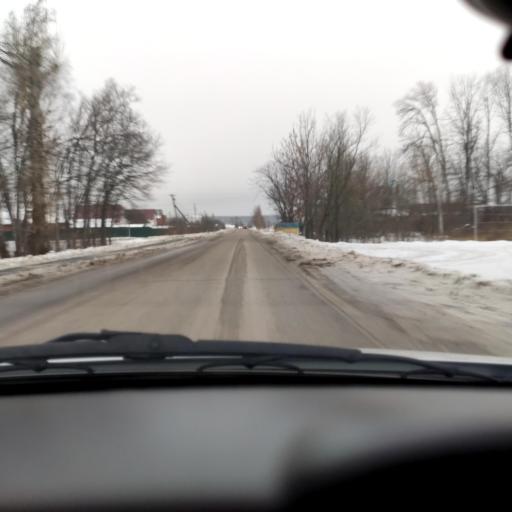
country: RU
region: Voronezj
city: Ramon'
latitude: 51.9137
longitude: 39.2888
